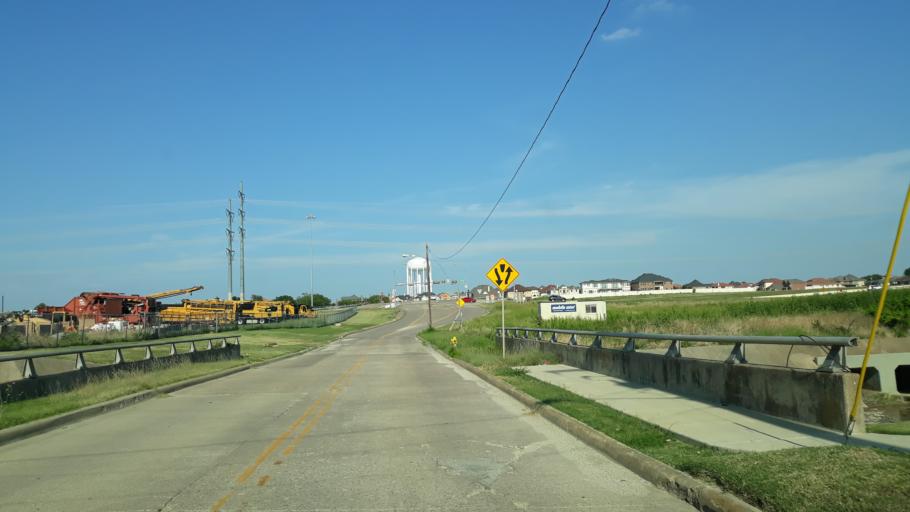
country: US
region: Texas
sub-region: Tarrant County
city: Euless
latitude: 32.8454
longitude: -97.0198
